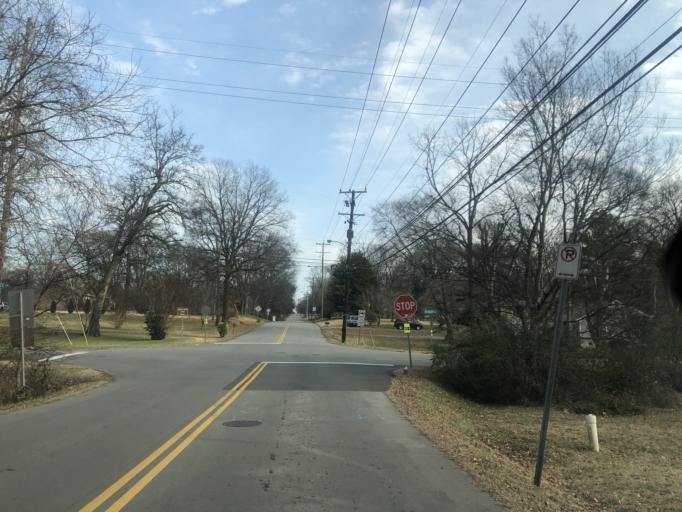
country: US
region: Tennessee
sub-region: Davidson County
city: Oak Hill
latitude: 36.1052
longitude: -86.7044
